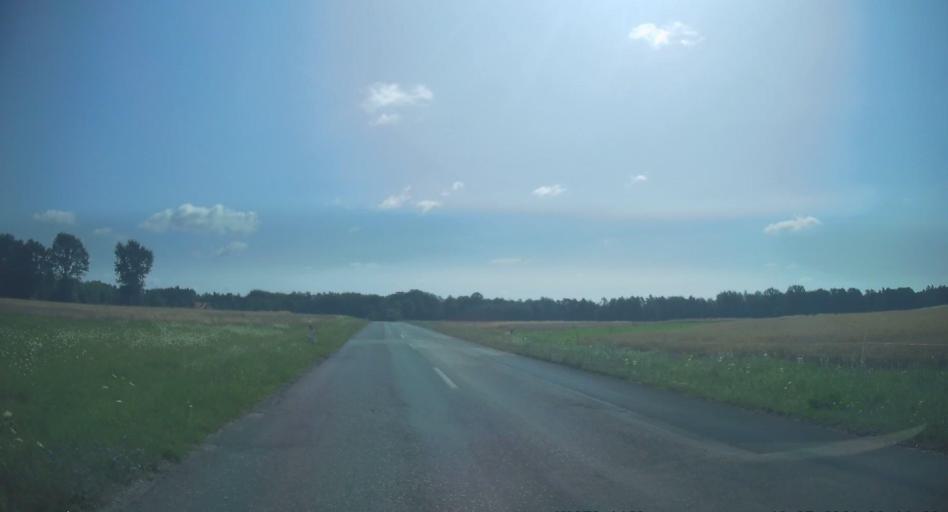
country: PL
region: Silesian Voivodeship
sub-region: Powiat gliwicki
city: Sosnicowice
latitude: 50.2794
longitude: 18.4803
